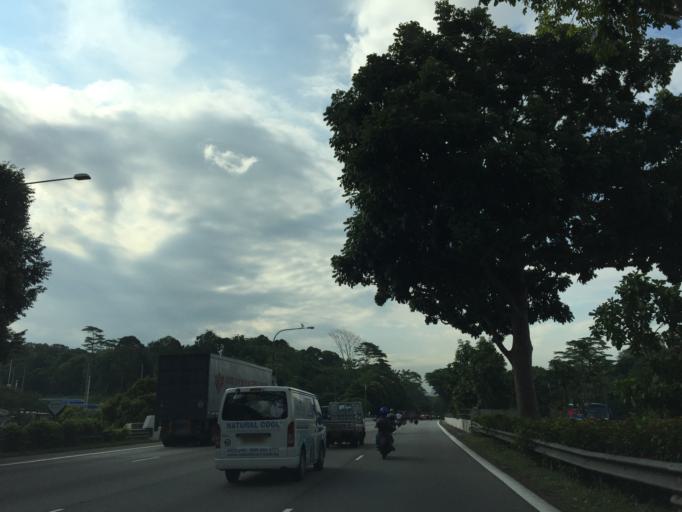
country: MY
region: Johor
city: Johor Bahru
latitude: 1.4091
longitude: 103.7718
